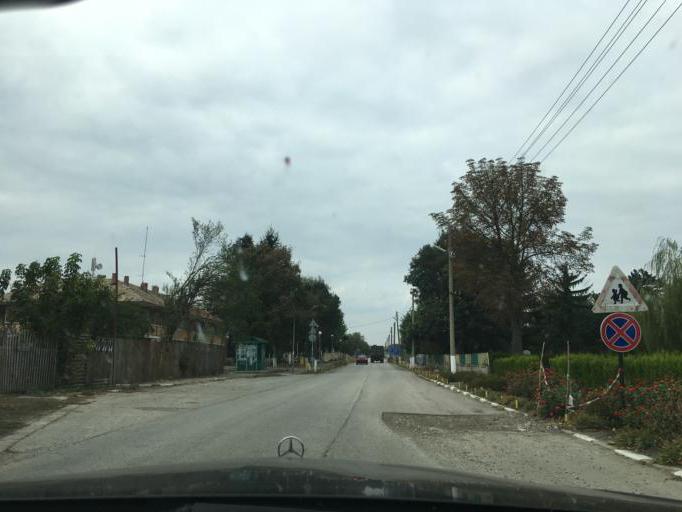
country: BG
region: Dobrich
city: General-Toshevo
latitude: 43.5743
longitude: 28.0802
